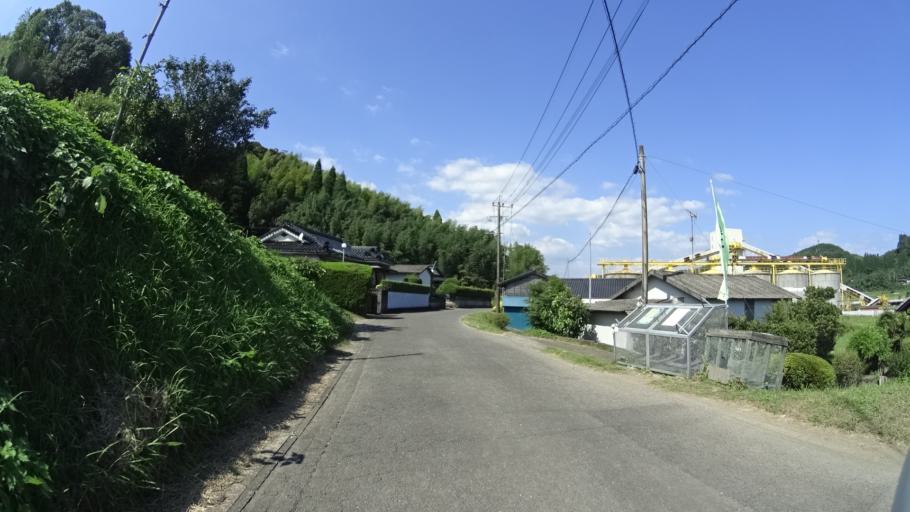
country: JP
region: Kagoshima
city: Kajiki
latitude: 31.7561
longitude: 130.6746
